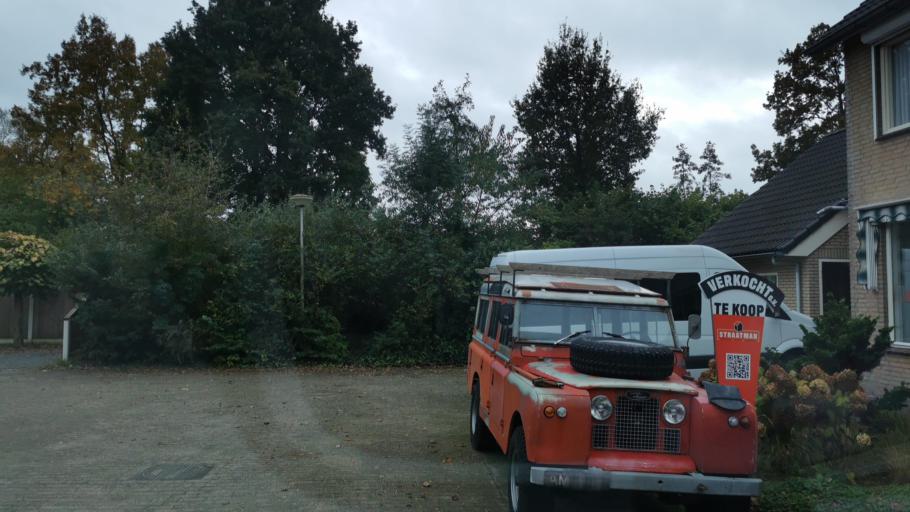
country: NL
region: Overijssel
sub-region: Gemeente Losser
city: Losser
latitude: 52.2520
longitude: 7.0082
